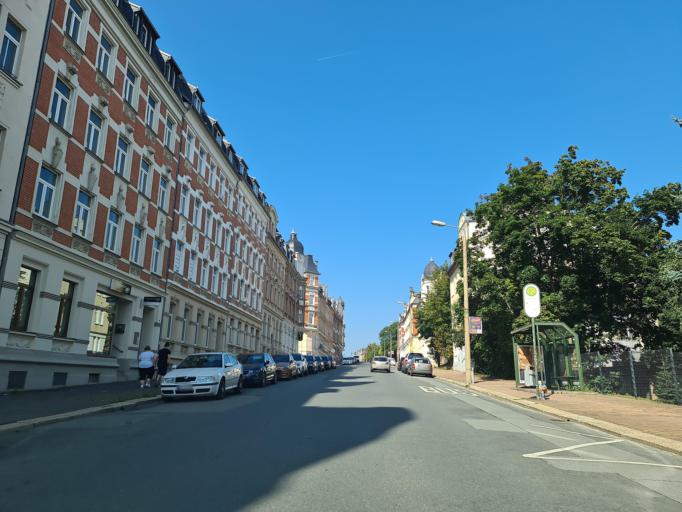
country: DE
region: Saxony
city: Plauen
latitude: 50.5089
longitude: 12.1450
